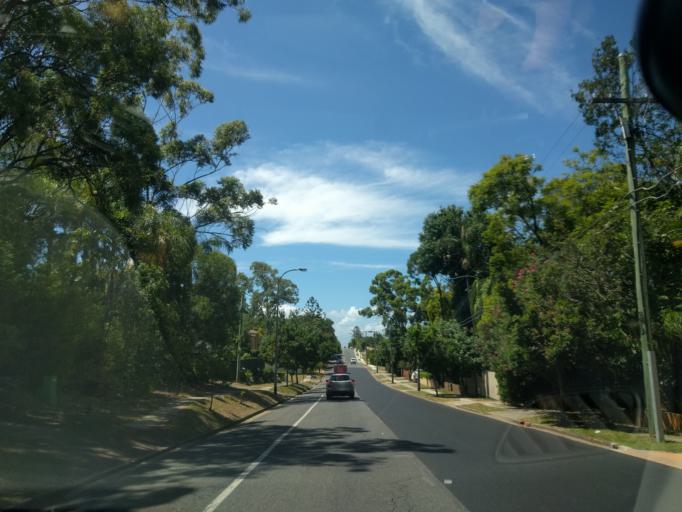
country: AU
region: Queensland
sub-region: Brisbane
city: Chermside West
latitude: -27.3742
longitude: 153.0145
